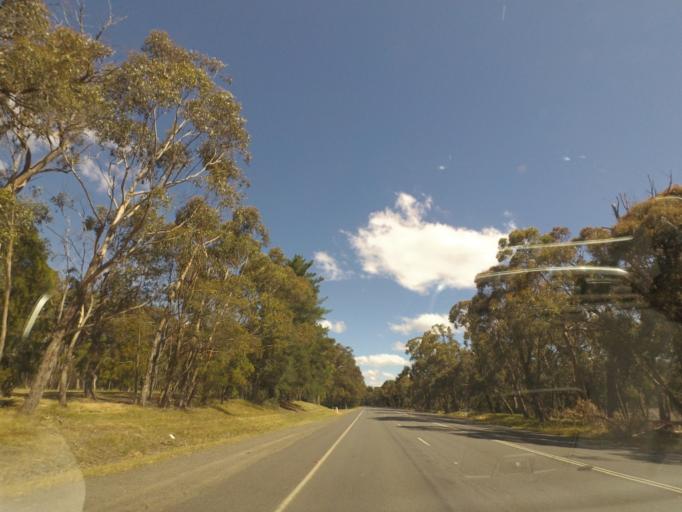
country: AU
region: Victoria
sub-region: Hume
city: Sunbury
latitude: -37.4253
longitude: 144.5541
